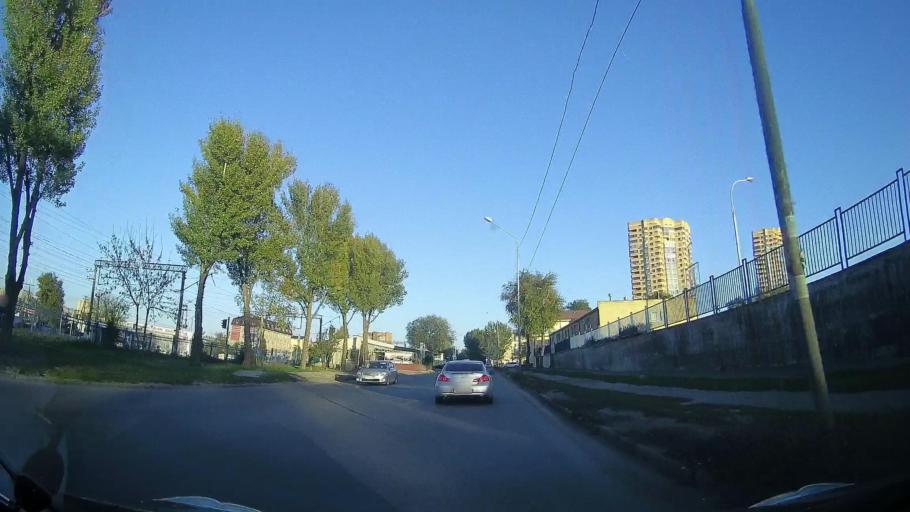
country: RU
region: Rostov
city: Rostov-na-Donu
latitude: 47.2446
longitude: 39.6986
